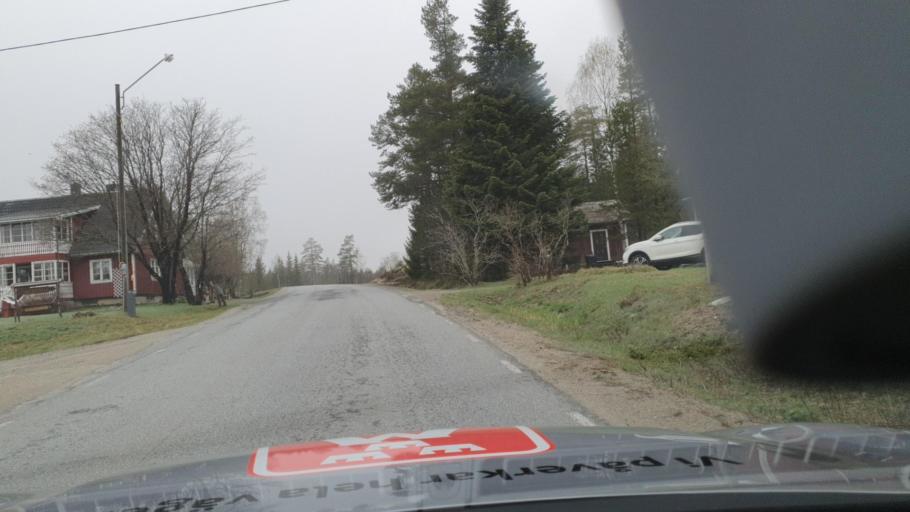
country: SE
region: Vaesternorrland
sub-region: OErnskoeldsviks Kommun
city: Husum
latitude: 63.4808
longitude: 19.2137
